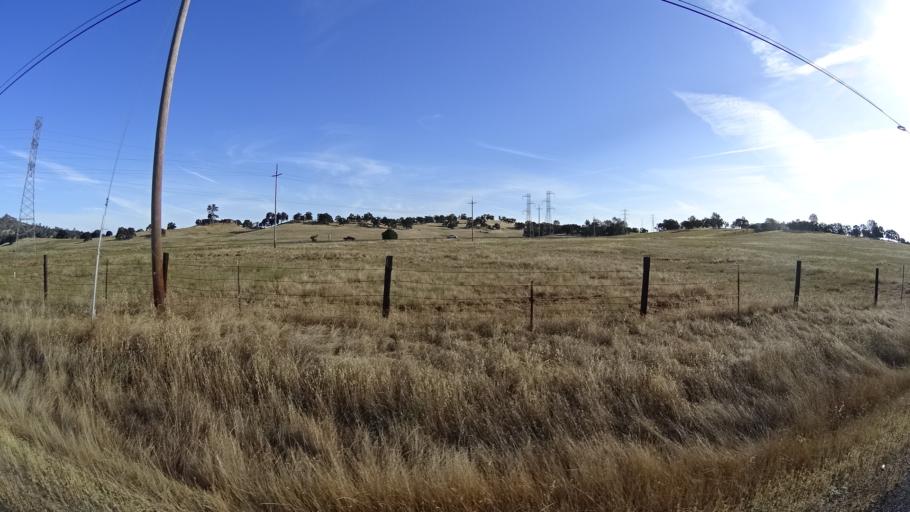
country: US
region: California
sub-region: Calaveras County
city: Valley Springs
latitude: 38.1924
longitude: -120.8157
